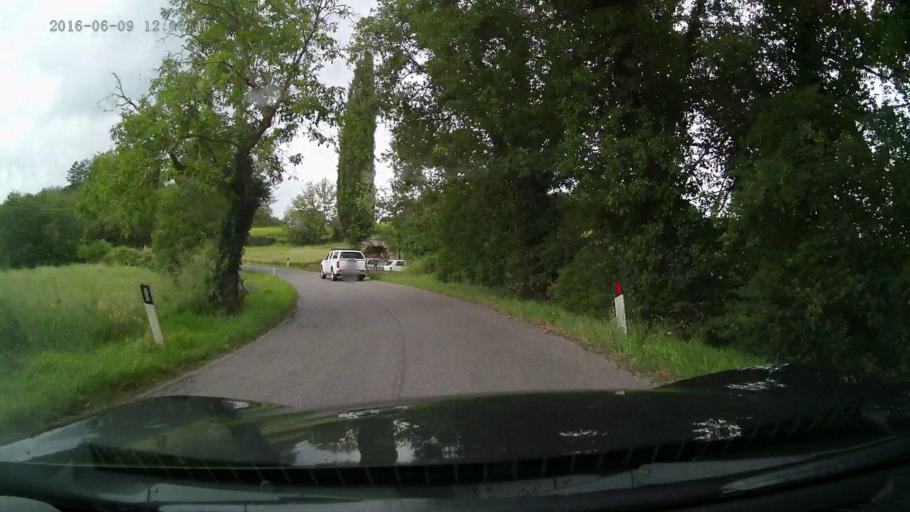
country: IT
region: Tuscany
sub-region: Province of Florence
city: Panzano in Chianti
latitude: 43.5270
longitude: 11.2897
